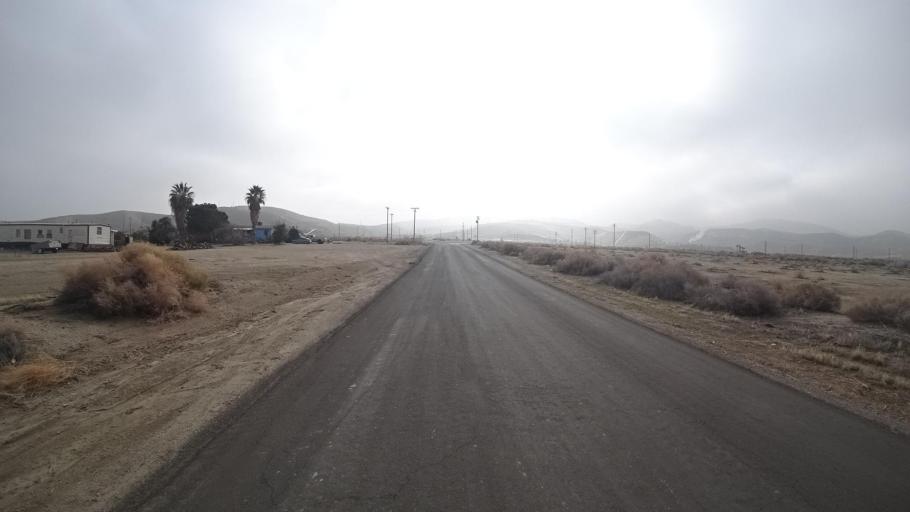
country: US
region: California
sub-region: Kern County
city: Maricopa
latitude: 35.0389
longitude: -119.3670
